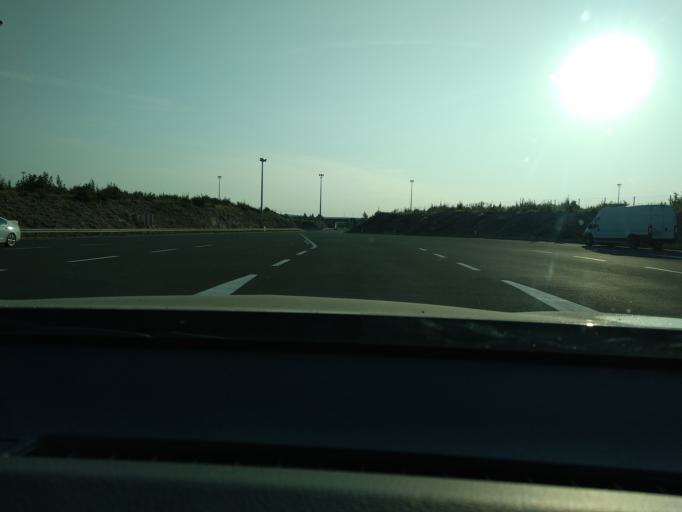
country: HR
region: Sibensko-Kniniska
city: Zaton
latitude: 43.8869
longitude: 15.7863
